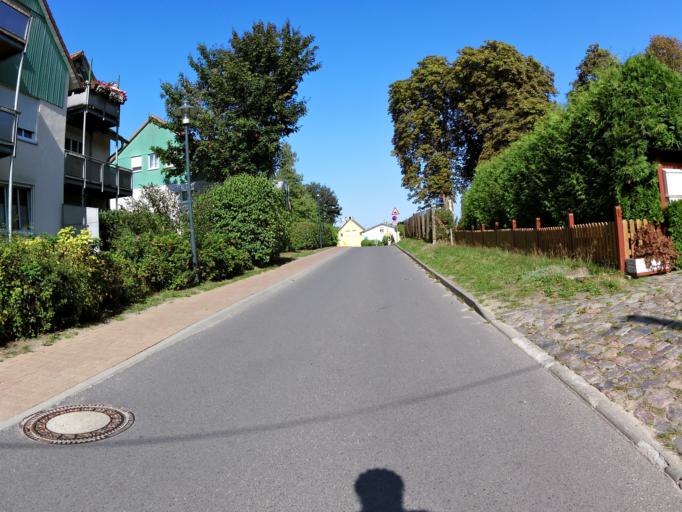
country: DE
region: Mecklenburg-Vorpommern
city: Seebad Heringsdorf
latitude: 53.9360
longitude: 14.1852
